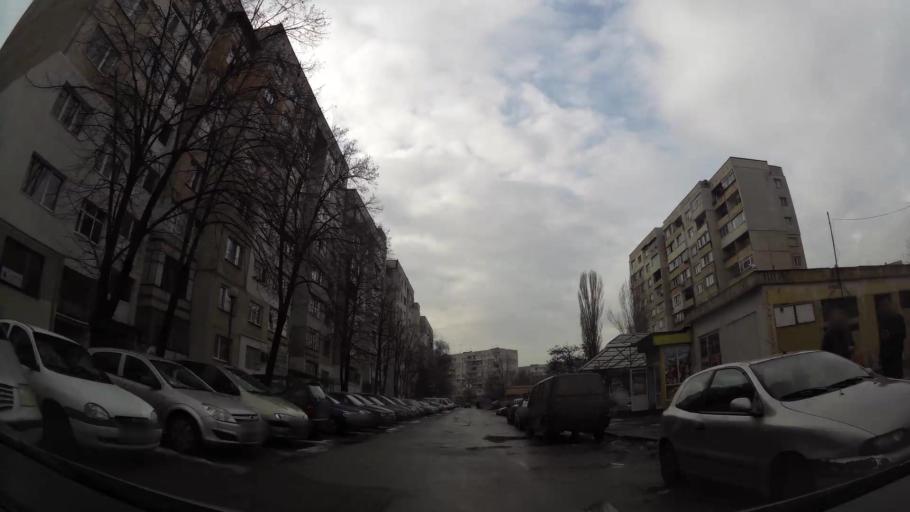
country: BG
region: Sofia-Capital
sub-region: Stolichna Obshtina
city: Sofia
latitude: 42.7141
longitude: 23.2621
